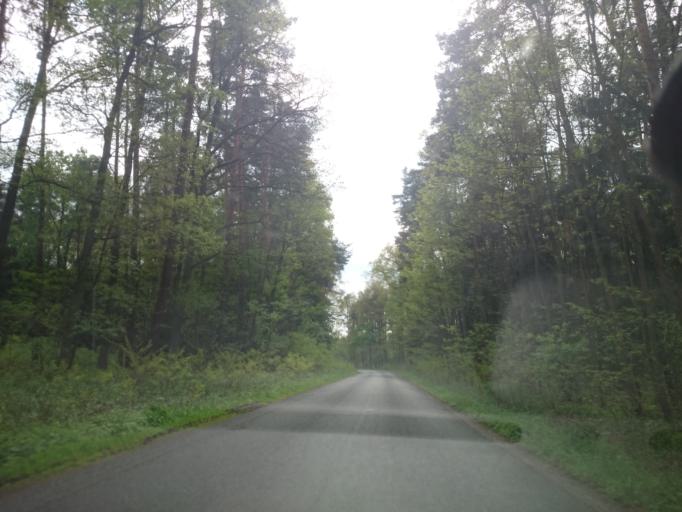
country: PL
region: Lower Silesian Voivodeship
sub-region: Powiat olesnicki
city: Dobroszyce
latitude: 51.3760
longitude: 17.2977
